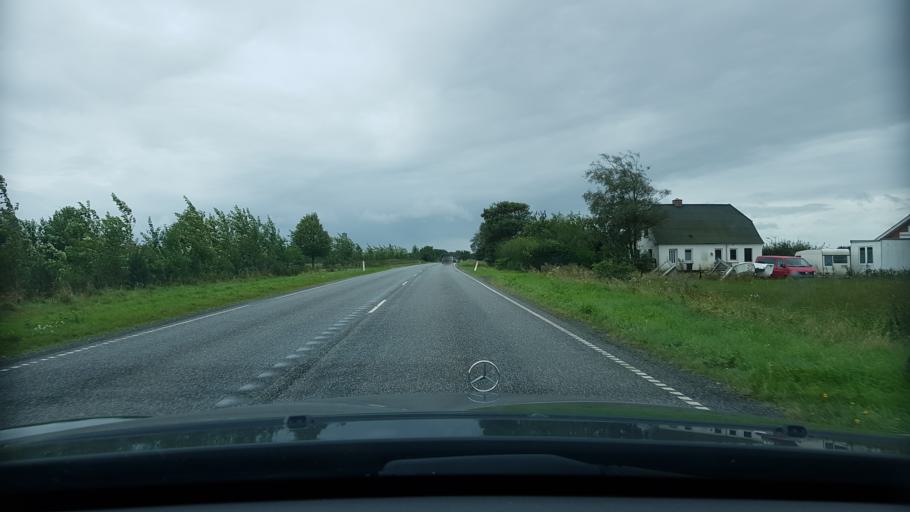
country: DK
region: Central Jutland
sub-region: Randers Kommune
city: Spentrup
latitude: 56.5497
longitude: 10.1029
